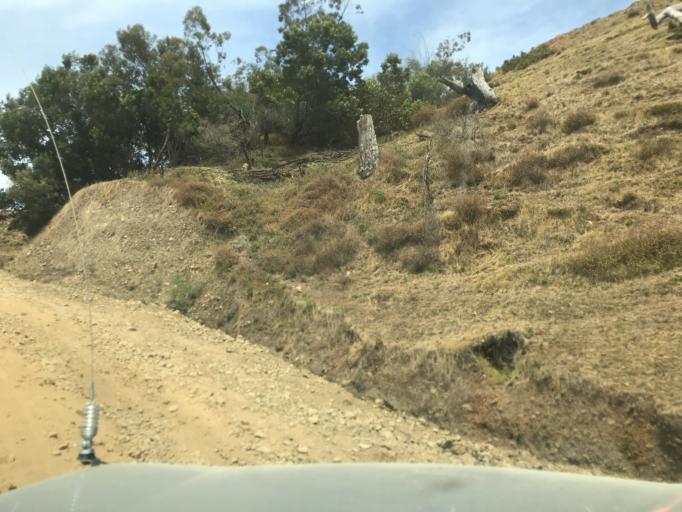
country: TL
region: Ainaro
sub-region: Ainaro
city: Ainaro
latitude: -8.8727
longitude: 125.5254
